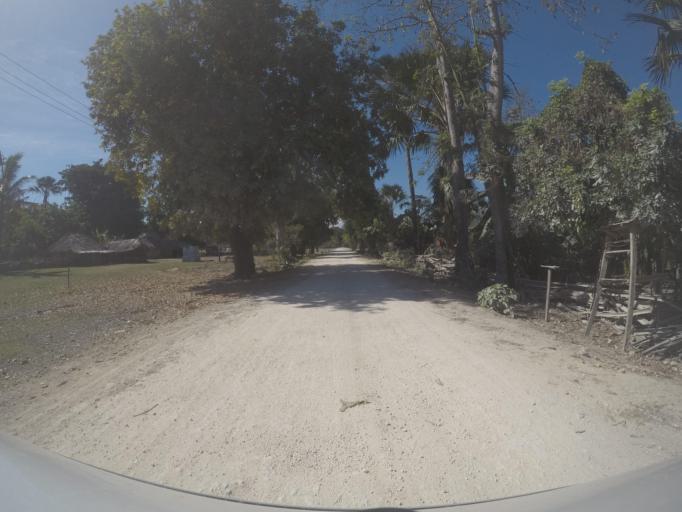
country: TL
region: Viqueque
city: Viqueque
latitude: -8.9012
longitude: 126.5063
